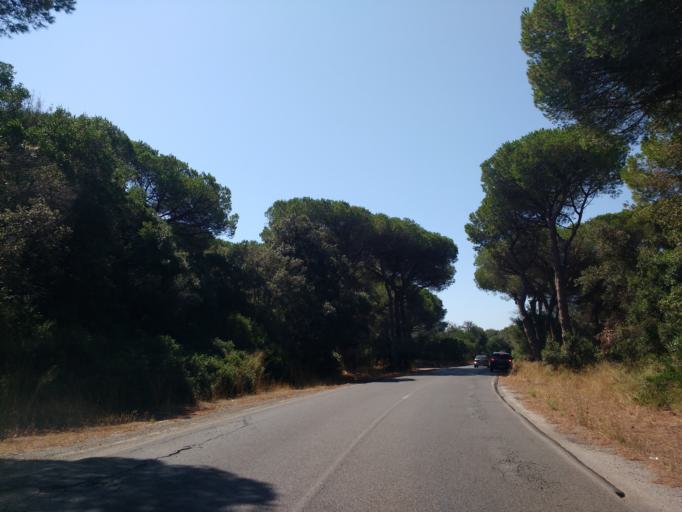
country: IT
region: Latium
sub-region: Citta metropolitana di Roma Capitale
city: Acilia-Castel Fusano-Ostia Antica
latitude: 41.7117
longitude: 12.3580
